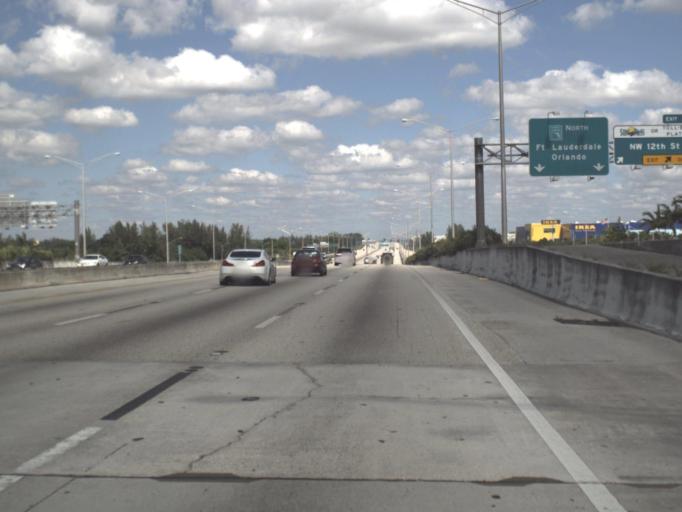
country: US
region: Florida
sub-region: Miami-Dade County
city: Sweetwater
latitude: 25.7828
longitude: -80.3857
